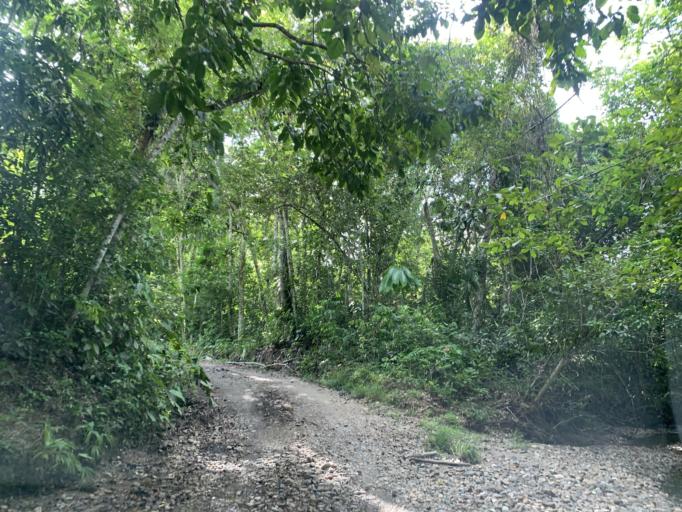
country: CO
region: Boyaca
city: Puerto Boyaca
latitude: 6.0102
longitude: -74.3899
